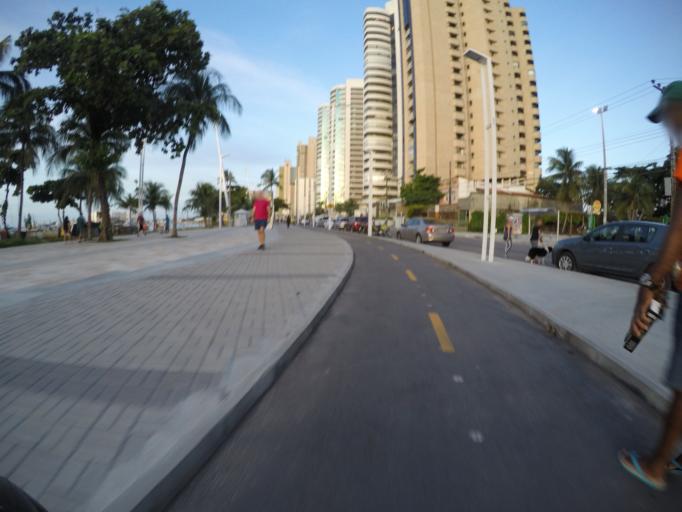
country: BR
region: Ceara
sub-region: Fortaleza
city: Fortaleza
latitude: -3.7230
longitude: -38.4838
